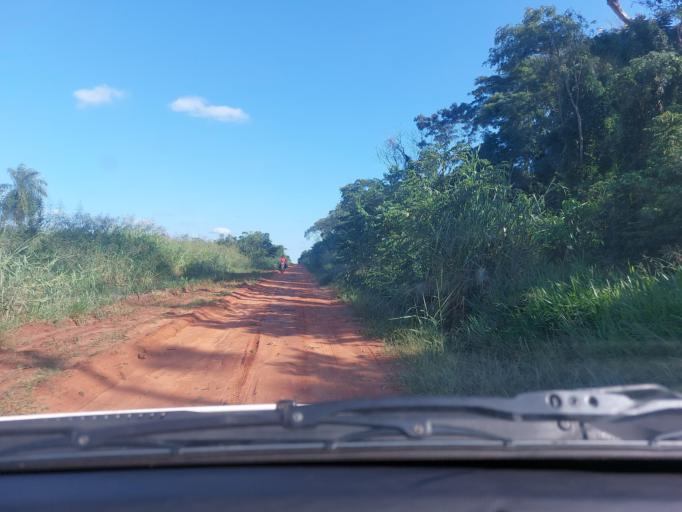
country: PY
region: San Pedro
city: Guayaybi
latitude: -24.5074
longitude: -56.5461
